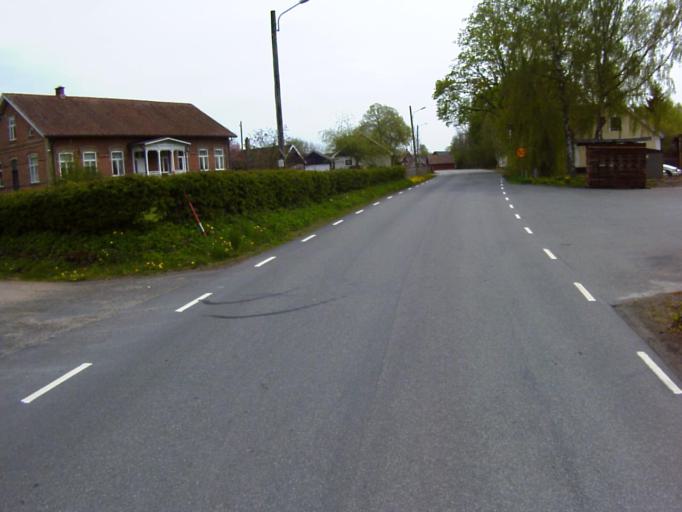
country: SE
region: Skane
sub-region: Kristianstads Kommun
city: Onnestad
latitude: 55.9448
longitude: 13.9488
